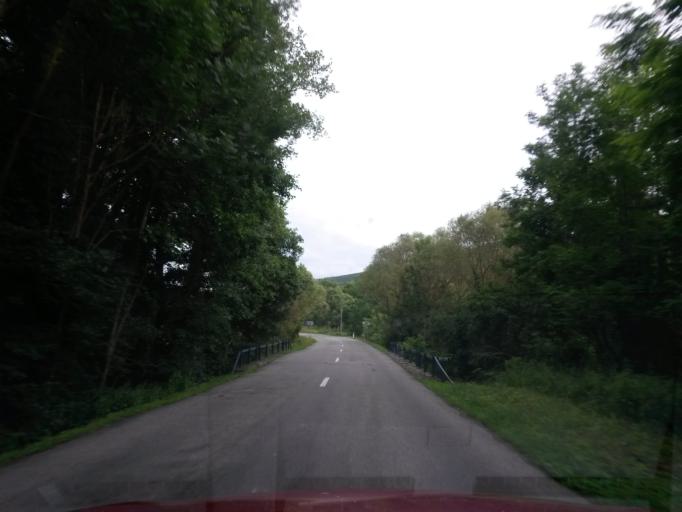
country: SK
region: Banskobystricky
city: Detva
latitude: 48.3886
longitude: 19.3788
